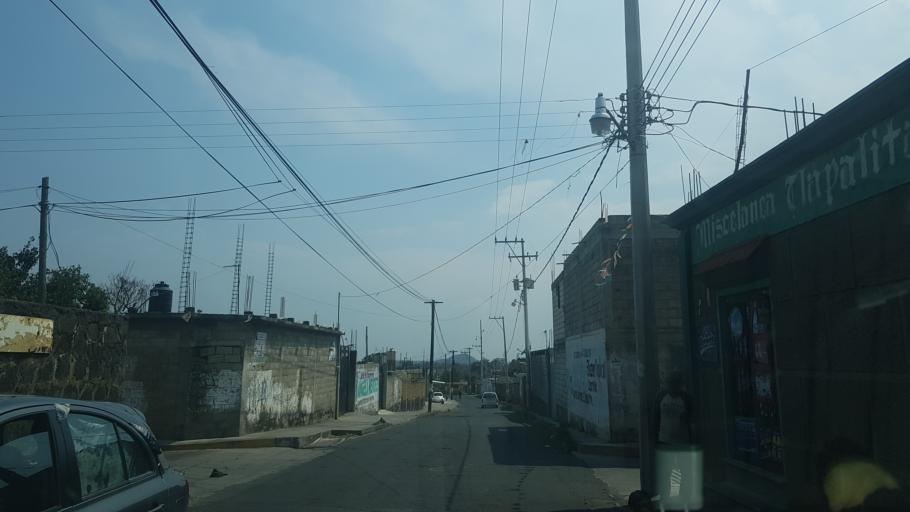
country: MX
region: Puebla
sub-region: Tianguismanalco
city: San Martin Tlapala
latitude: 18.9636
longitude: -98.4590
